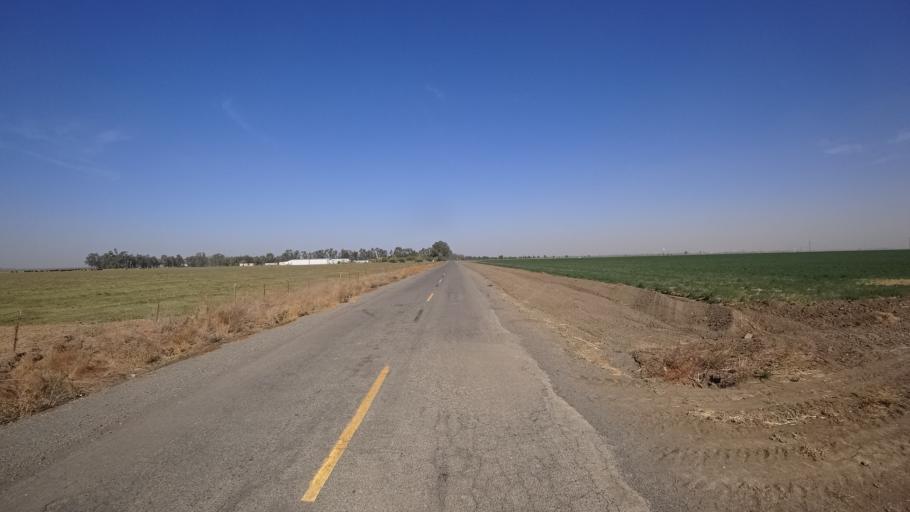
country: US
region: California
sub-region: Yolo County
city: Davis
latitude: 38.4813
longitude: -121.6937
